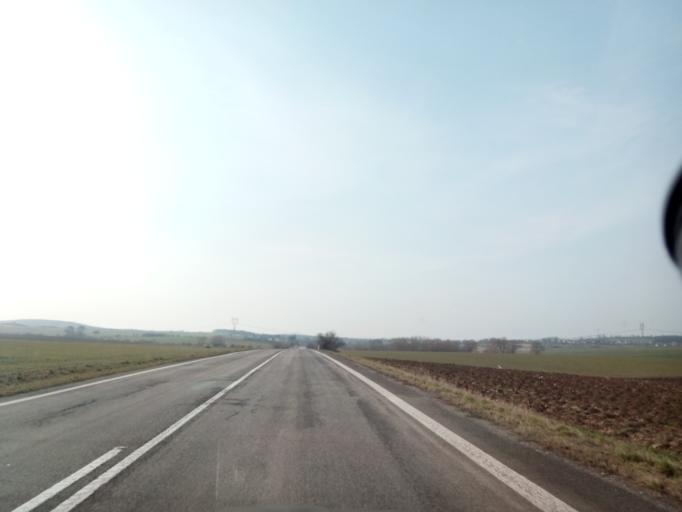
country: SK
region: Kosicky
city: Trebisov
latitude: 48.5354
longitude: 21.6784
